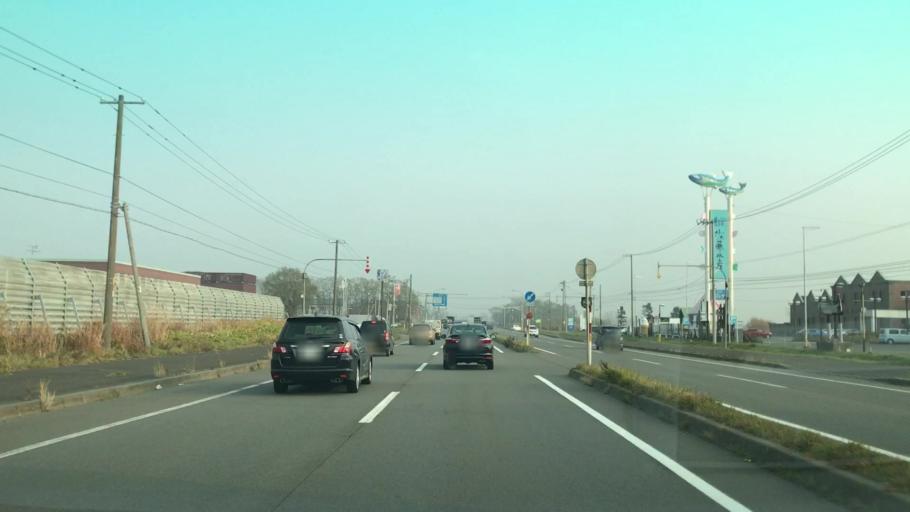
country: JP
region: Hokkaido
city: Ishikari
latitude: 43.2063
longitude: 141.3323
